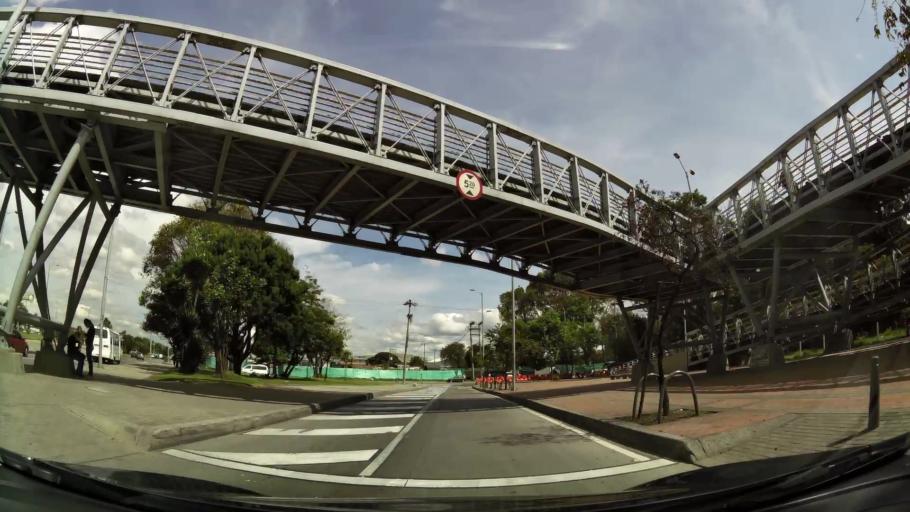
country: CO
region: Bogota D.C.
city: Bogota
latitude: 4.6855
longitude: -74.1239
